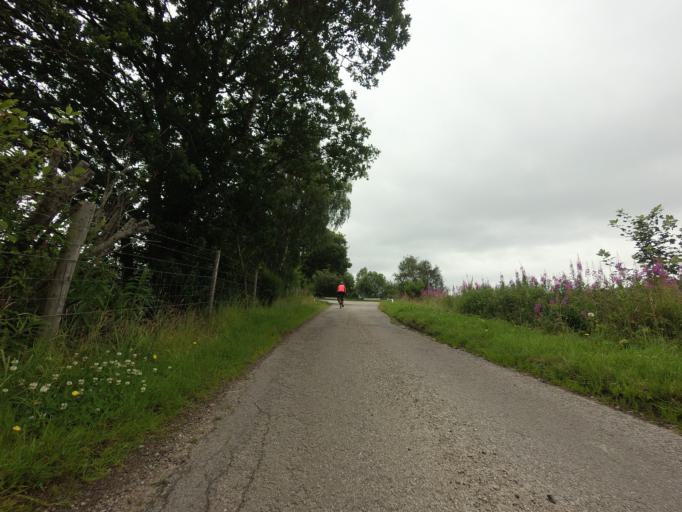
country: GB
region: Scotland
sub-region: Highland
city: Evanton
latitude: 57.9181
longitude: -4.4035
